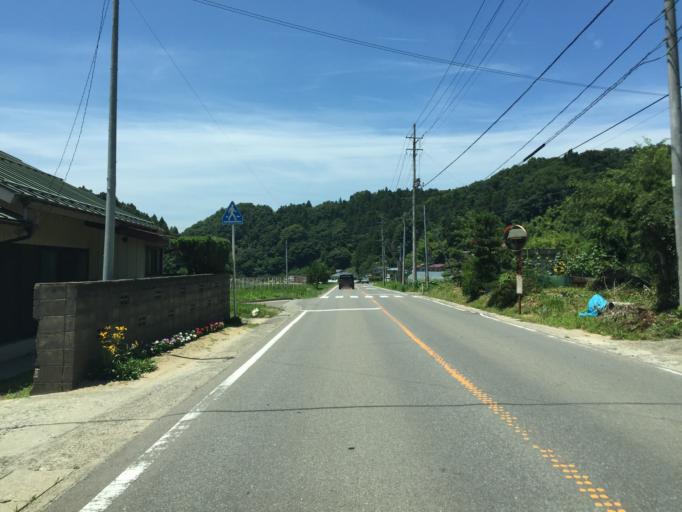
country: JP
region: Fukushima
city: Yanagawamachi-saiwaicho
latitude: 37.7599
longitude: 140.6422
